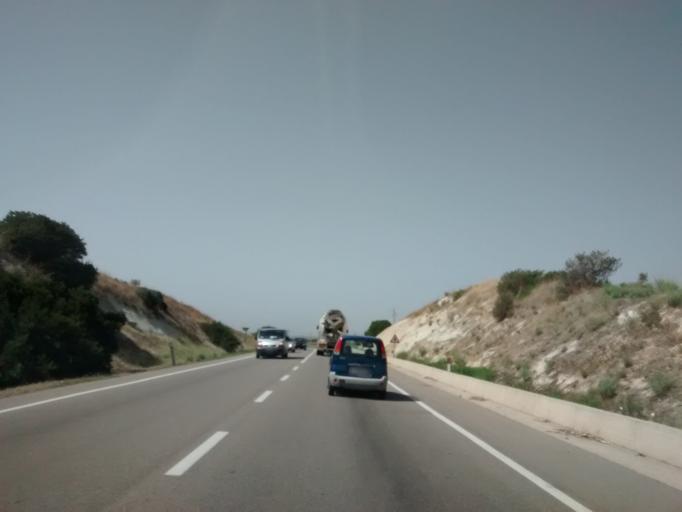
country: IT
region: Sardinia
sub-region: Provincia di Cagliari
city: Maracalagonis
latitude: 39.2691
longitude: 9.2081
